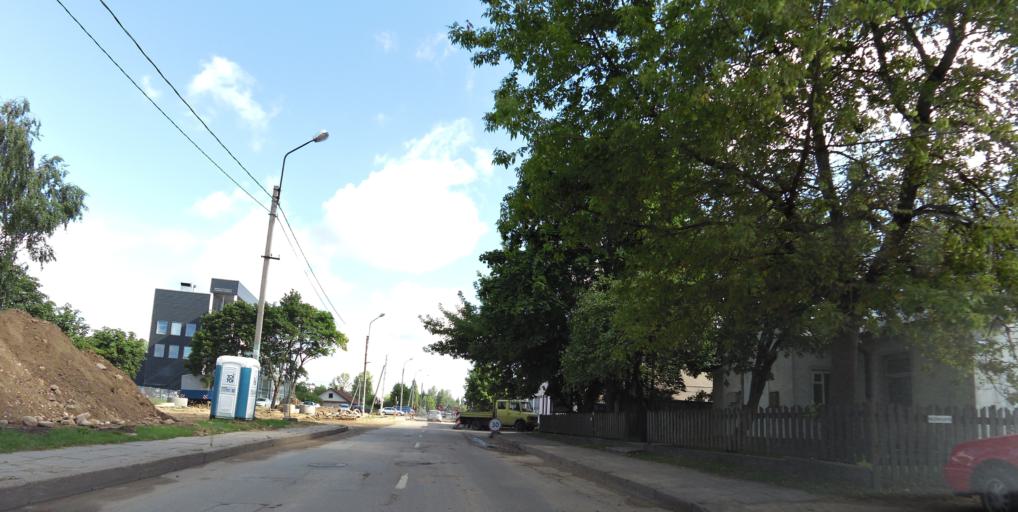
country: LT
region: Vilnius County
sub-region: Vilnius
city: Vilnius
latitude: 54.7029
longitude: 25.2702
